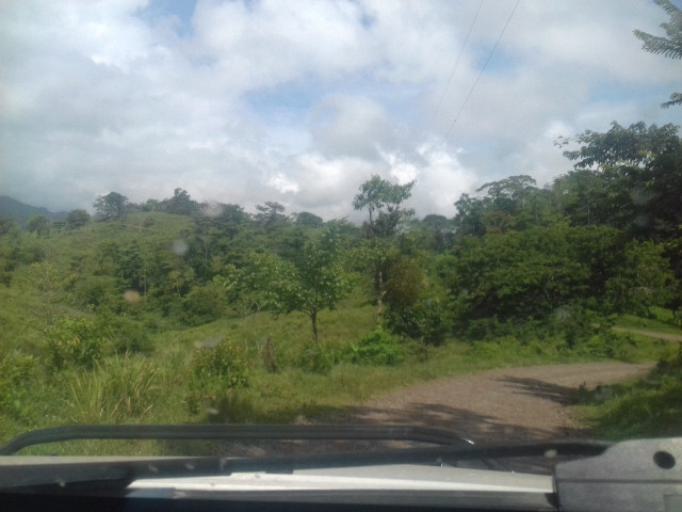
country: NI
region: Matagalpa
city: Matiguas
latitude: 12.9320
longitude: -85.3665
